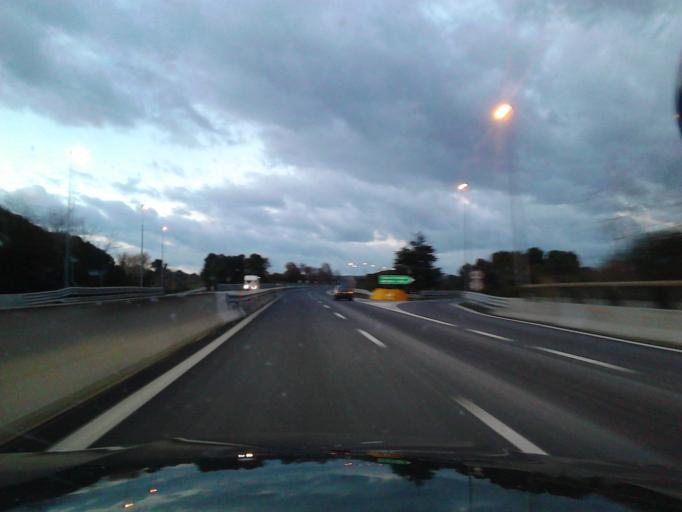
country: IT
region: Abruzzo
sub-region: Provincia di Teramo
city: Colleranesco
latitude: 42.7119
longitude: 13.9137
